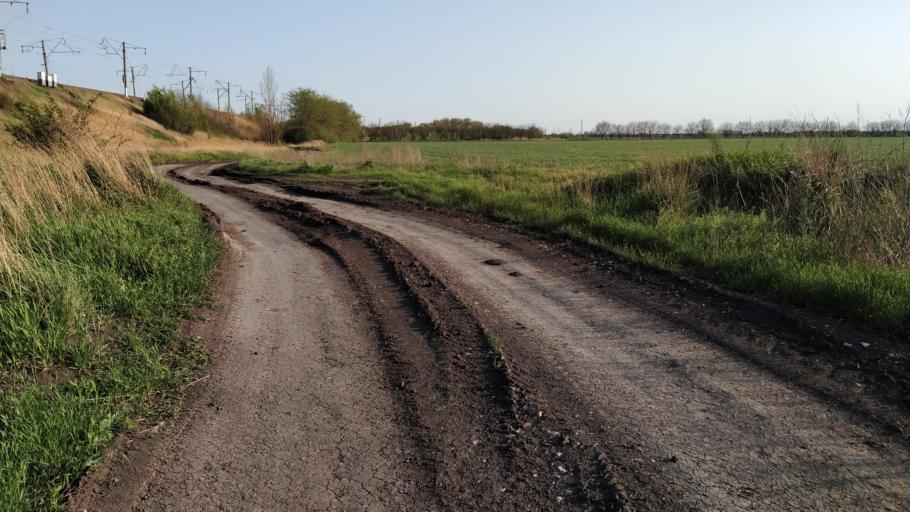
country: RU
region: Rostov
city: Bataysk
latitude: 47.0921
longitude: 39.7125
